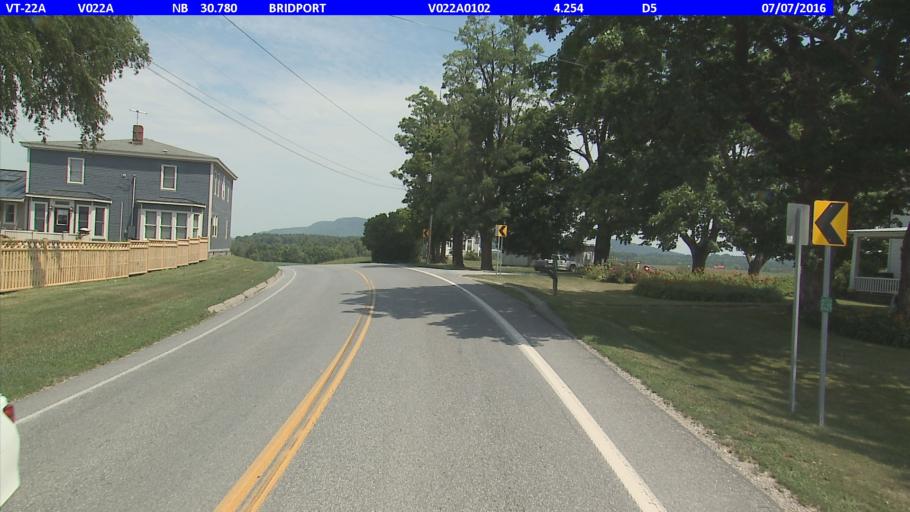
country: US
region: Vermont
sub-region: Addison County
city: Middlebury (village)
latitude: 44.0010
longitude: -73.3080
